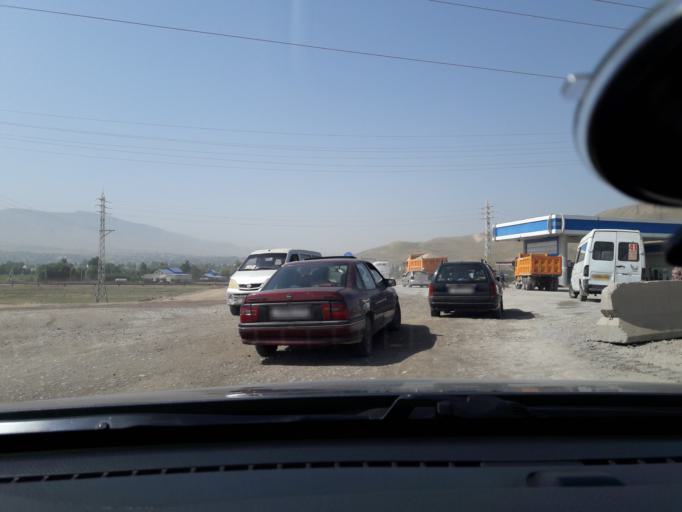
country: TJ
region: Dushanbe
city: Boshkengash
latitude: 38.4534
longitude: 68.7354
